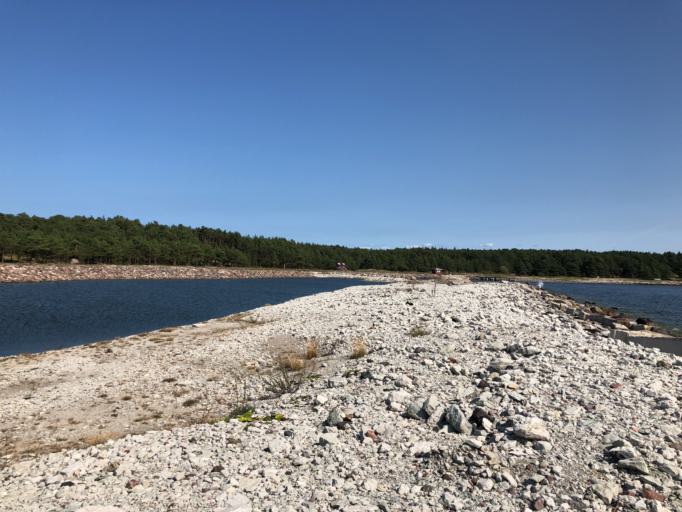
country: EE
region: Hiiumaa
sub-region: Kaerdla linn
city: Kardla
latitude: 58.9209
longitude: 22.0580
